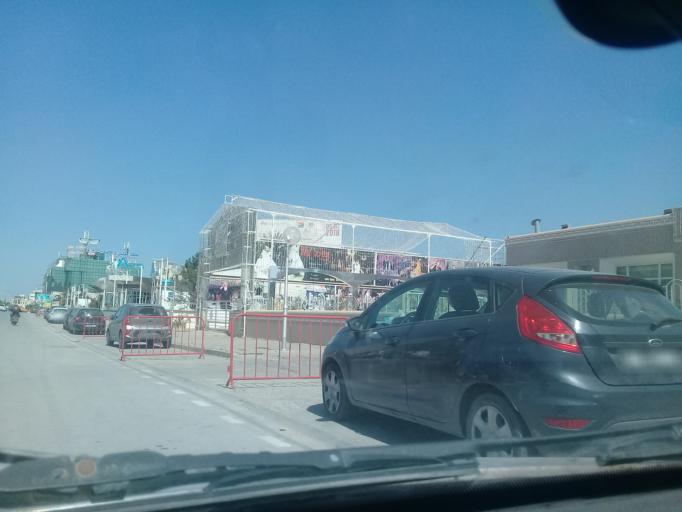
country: TN
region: Ariana
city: Ariana
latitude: 36.8334
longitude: 10.2335
